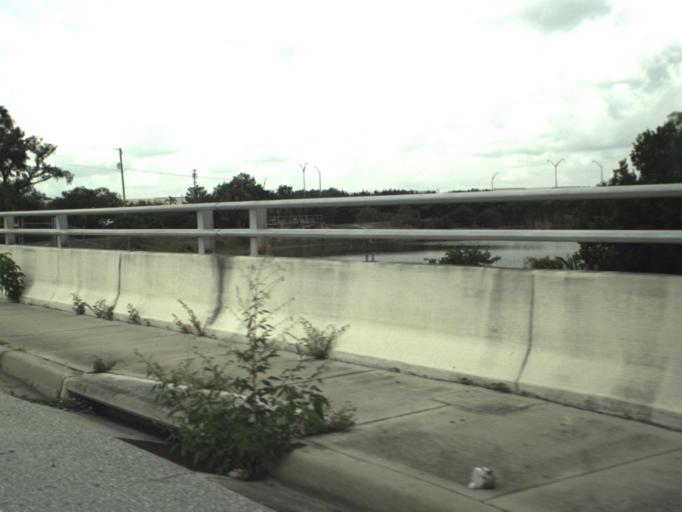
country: US
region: Florida
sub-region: Palm Beach County
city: West Palm Beach
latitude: 26.7013
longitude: -80.0695
